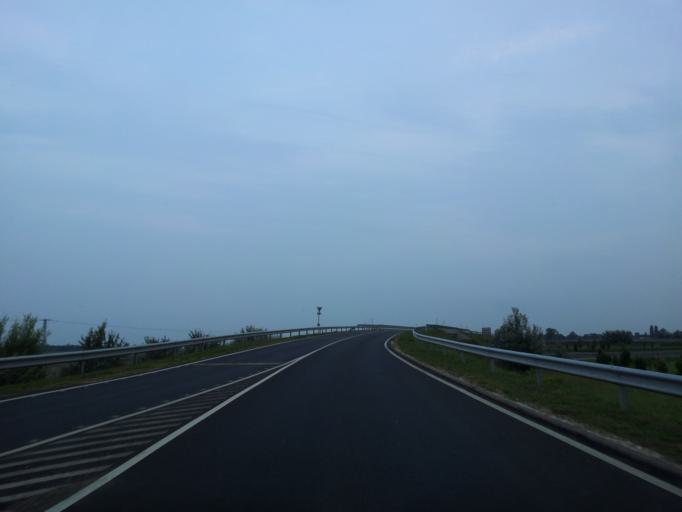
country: HU
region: Tolna
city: Tolna
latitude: 46.4098
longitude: 18.7360
